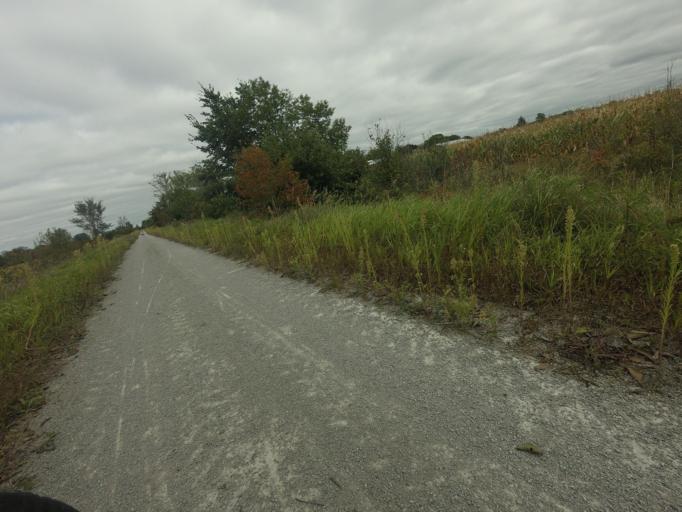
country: CA
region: Ontario
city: Uxbridge
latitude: 44.3100
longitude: -78.8830
